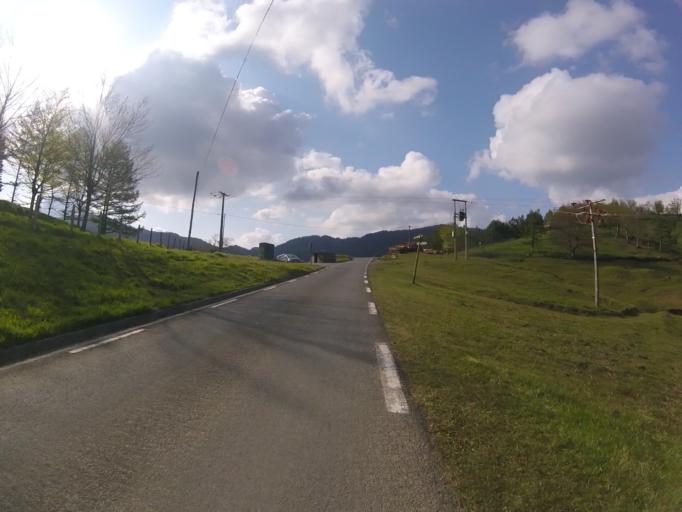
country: ES
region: Basque Country
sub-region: Provincia de Guipuzcoa
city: Azkoitia
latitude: 43.2189
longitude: -2.3108
